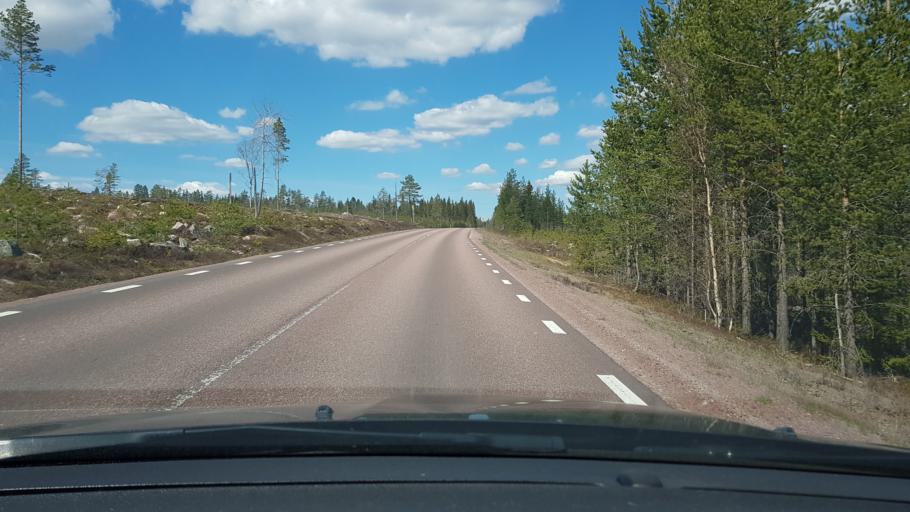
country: SE
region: Dalarna
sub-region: Malung-Saelens kommun
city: Malung
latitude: 61.0725
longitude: 13.6386
